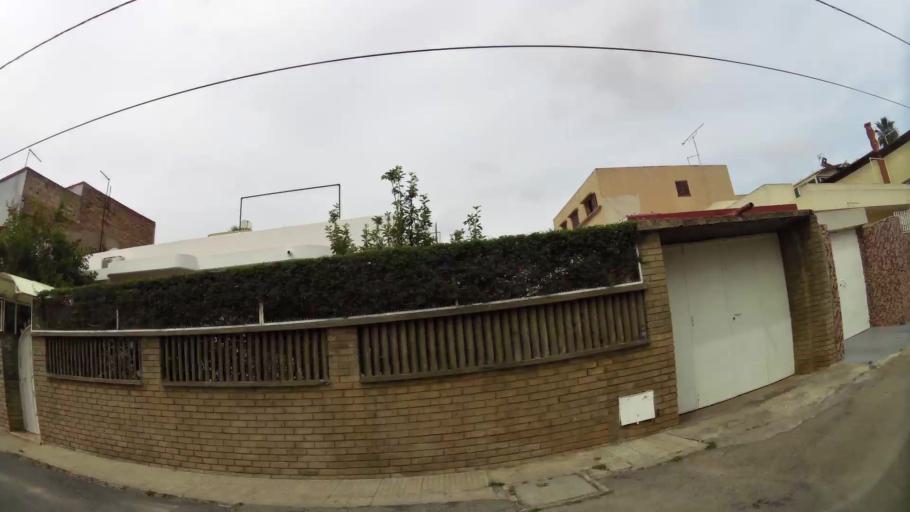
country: MA
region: Rabat-Sale-Zemmour-Zaer
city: Sale
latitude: 34.0280
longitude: -6.8085
